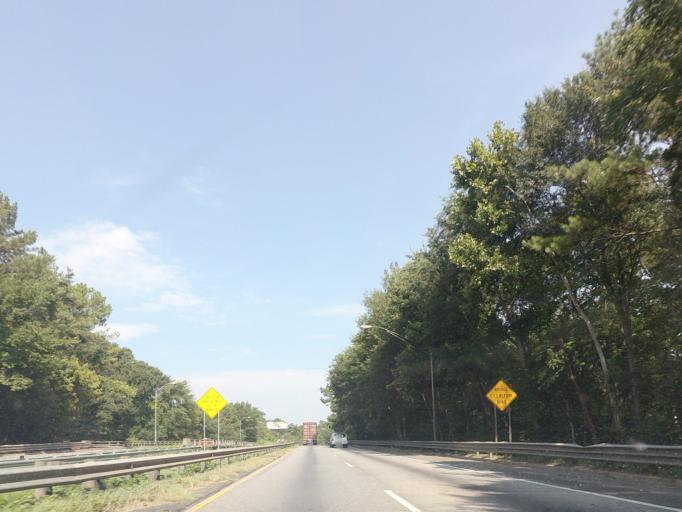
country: US
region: Georgia
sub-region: Bibb County
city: Macon
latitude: 32.8626
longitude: -83.6495
